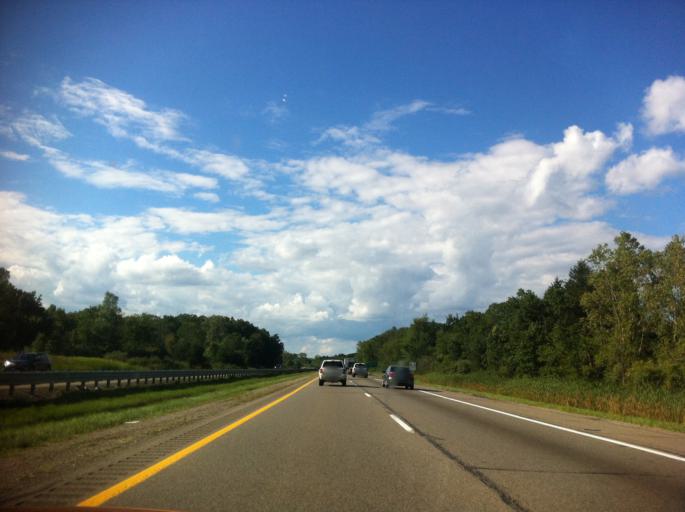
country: US
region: Michigan
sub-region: Livingston County
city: Whitmore Lake
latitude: 42.3607
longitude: -83.7488
